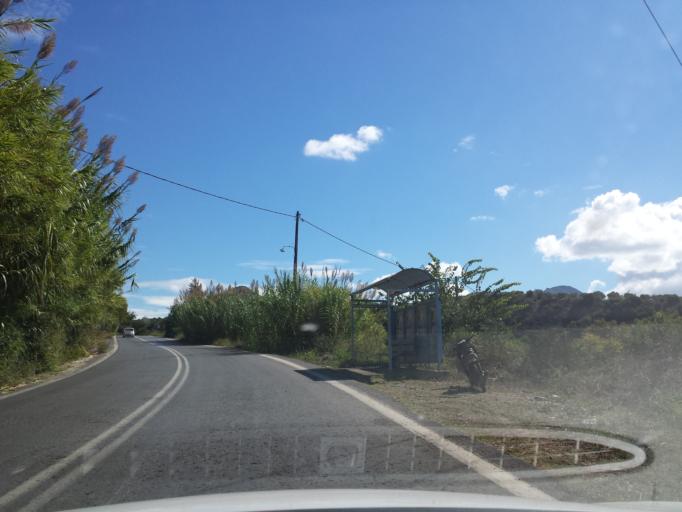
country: GR
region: Peloponnese
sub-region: Nomos Messinias
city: Pylos
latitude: 36.9507
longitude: 21.7594
